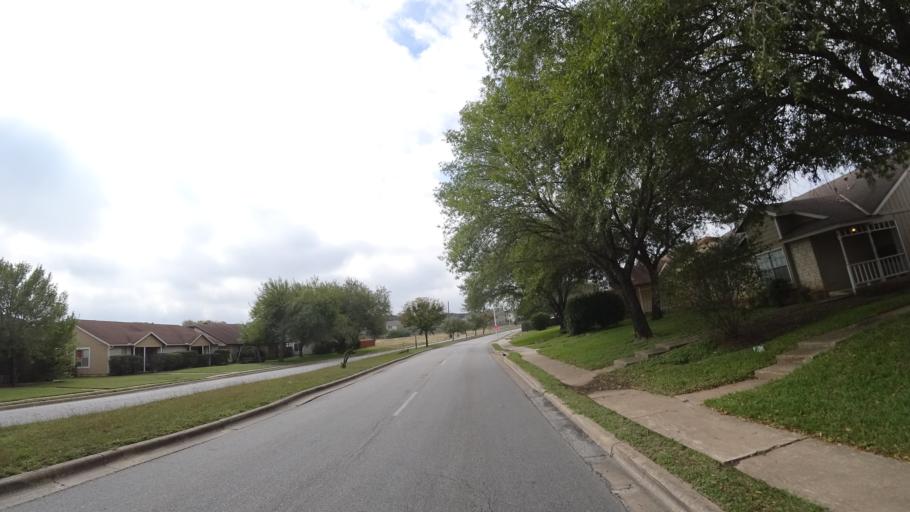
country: US
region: Texas
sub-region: Travis County
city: Shady Hollow
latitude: 30.1971
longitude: -97.8287
